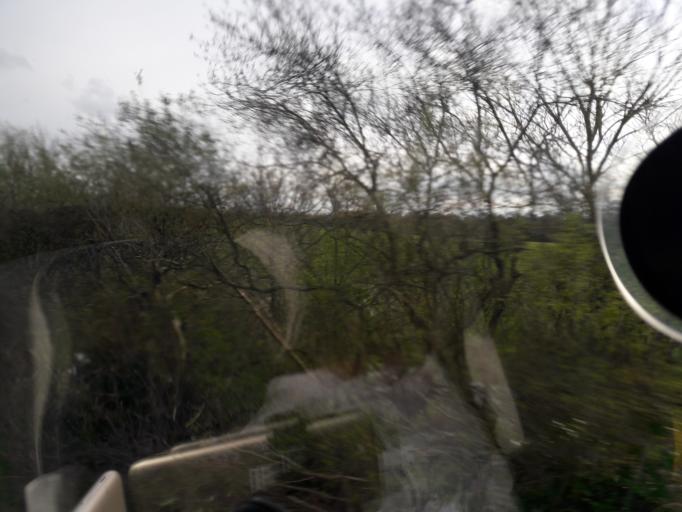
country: IE
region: Leinster
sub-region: An Mhi
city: Longwood
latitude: 53.4631
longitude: -6.9701
